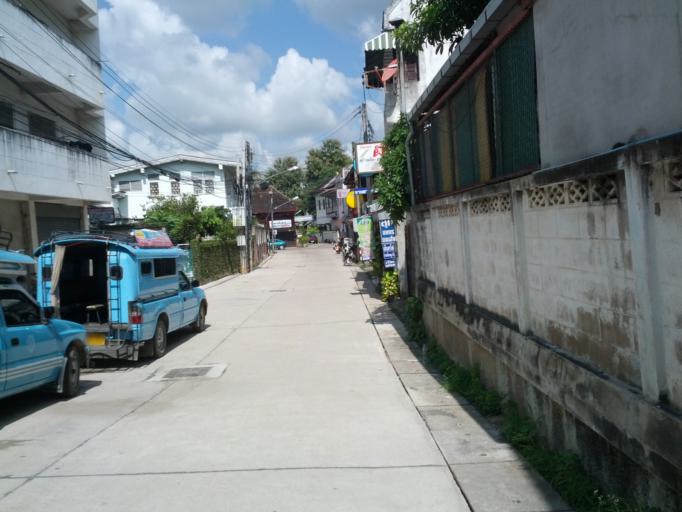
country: TH
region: Lampang
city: Lampang
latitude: 18.2902
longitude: 99.4983
